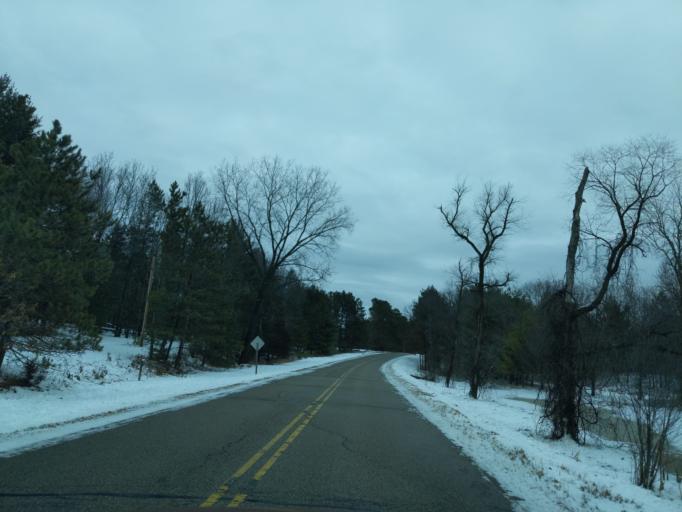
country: US
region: Wisconsin
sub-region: Marquette County
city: Montello
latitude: 43.9095
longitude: -89.3675
